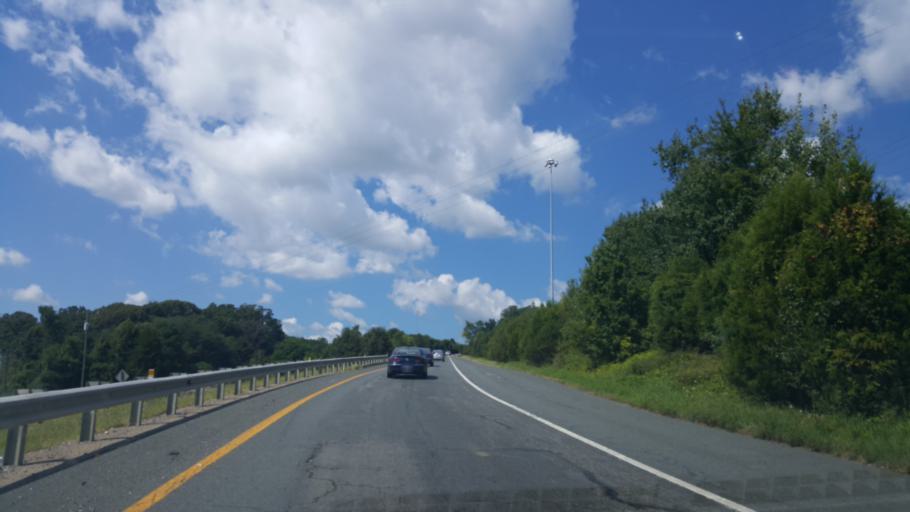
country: US
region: Virginia
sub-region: Prince William County
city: Woodbridge
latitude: 38.6772
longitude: -77.2306
